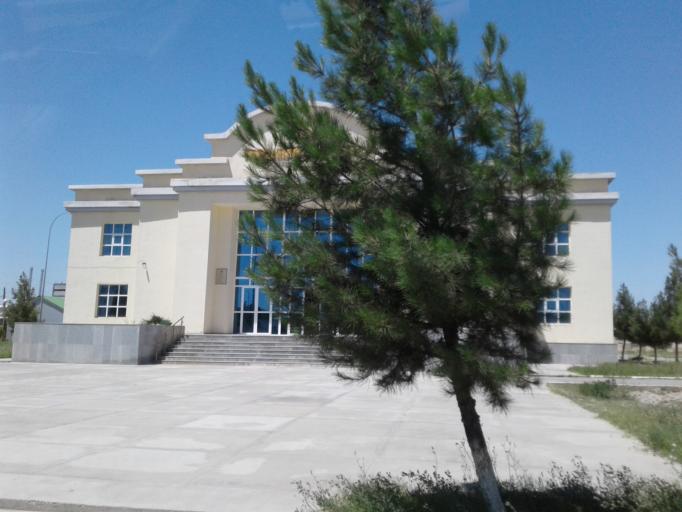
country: TM
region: Mary
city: Mary
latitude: 37.6054
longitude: 61.9238
